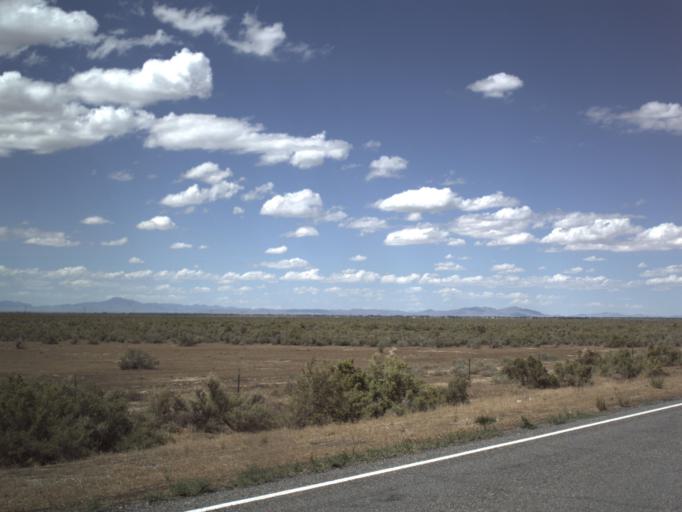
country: US
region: Utah
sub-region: Millard County
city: Delta
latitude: 39.2435
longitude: -112.4350
